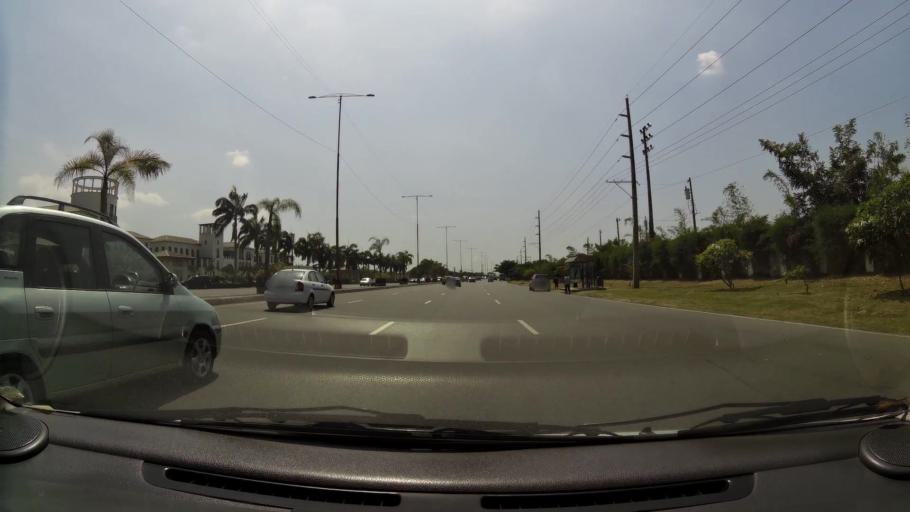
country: EC
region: Guayas
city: Eloy Alfaro
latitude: -2.0992
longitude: -79.8738
